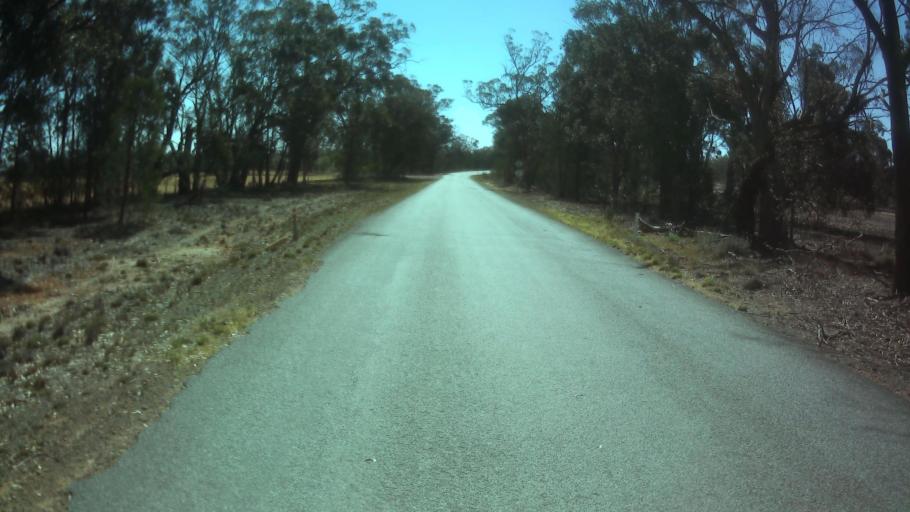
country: AU
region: New South Wales
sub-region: Weddin
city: Grenfell
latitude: -33.8066
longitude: 147.9009
